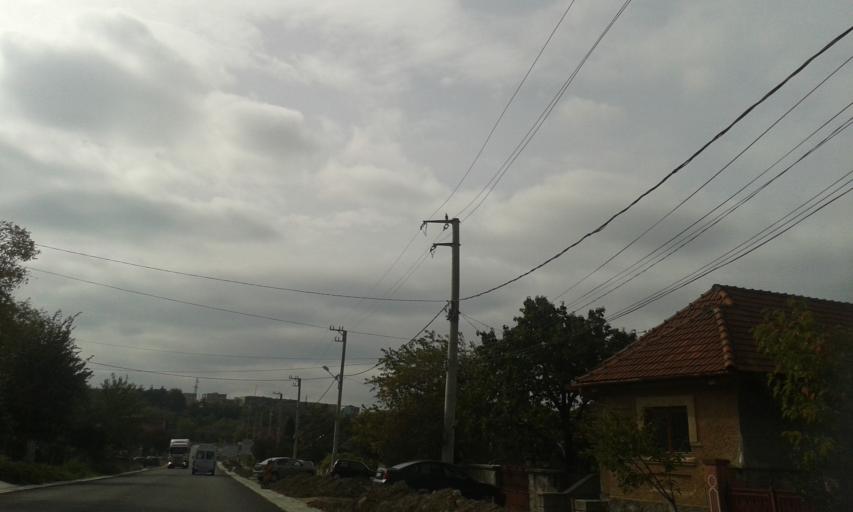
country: RO
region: Gorj
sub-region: Comuna Bumbesti-Jiu
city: Bumbesti-Jiu
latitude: 45.1860
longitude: 23.3867
